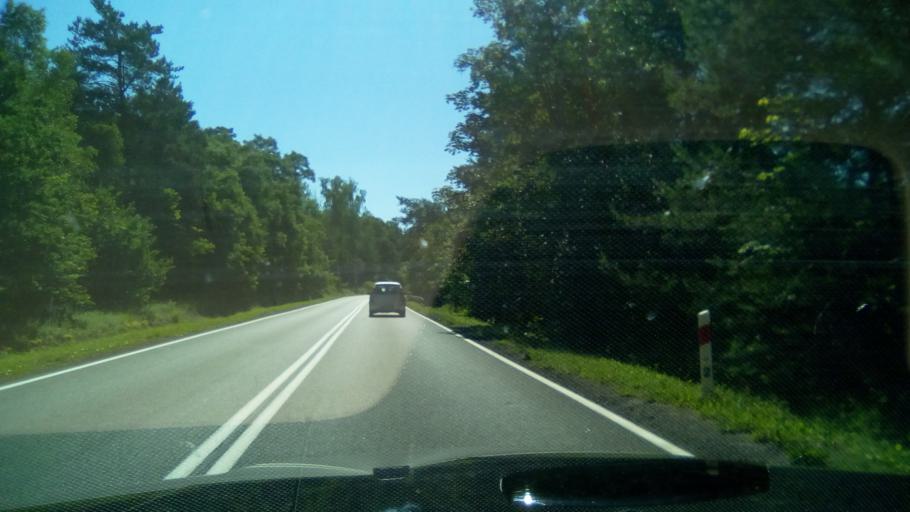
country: PL
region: Lodz Voivodeship
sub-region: Powiat tomaszowski
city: Inowlodz
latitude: 51.5247
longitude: 20.1957
